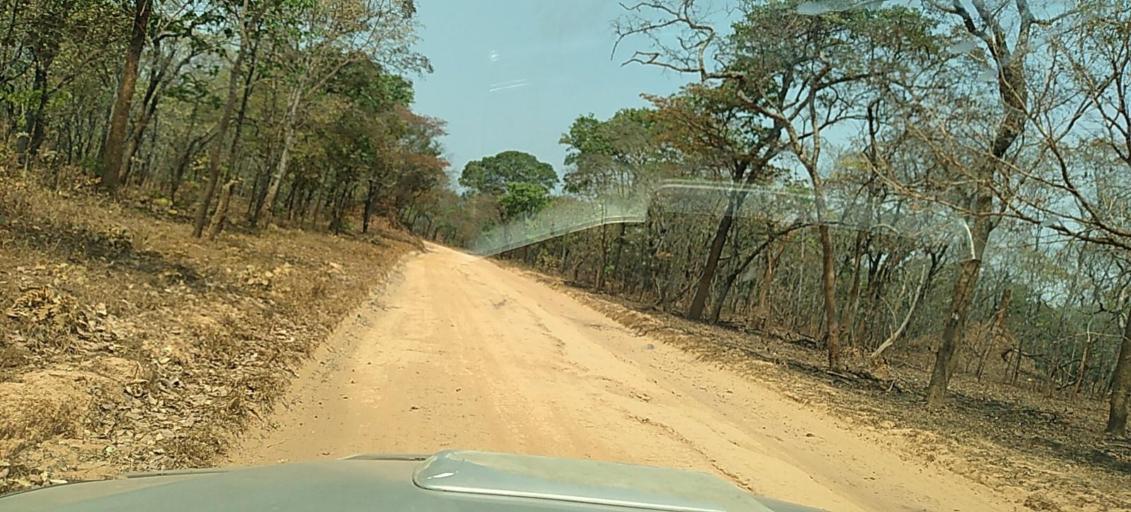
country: ZM
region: North-Western
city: Kasempa
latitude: -13.6584
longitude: 26.2650
